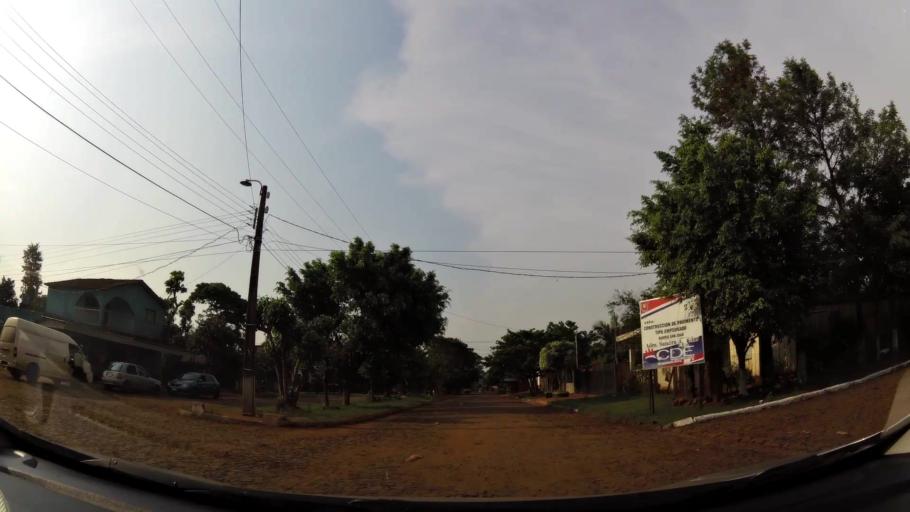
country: PY
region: Alto Parana
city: Ciudad del Este
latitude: -25.4806
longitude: -54.6685
